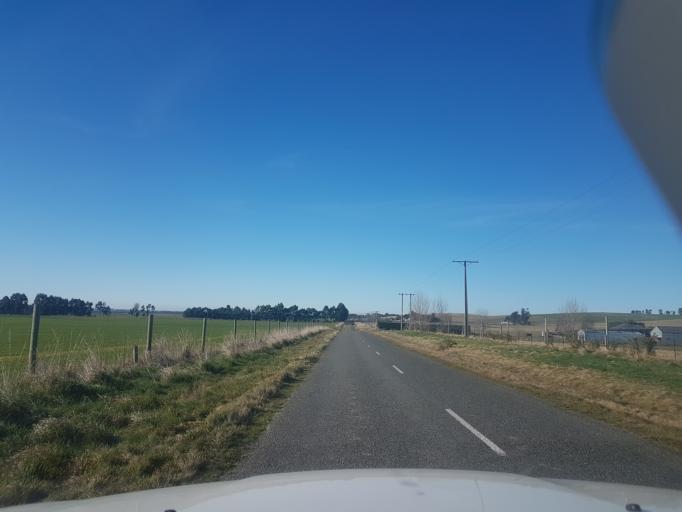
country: NZ
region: Canterbury
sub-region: Timaru District
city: Pleasant Point
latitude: -44.2919
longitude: 171.0574
